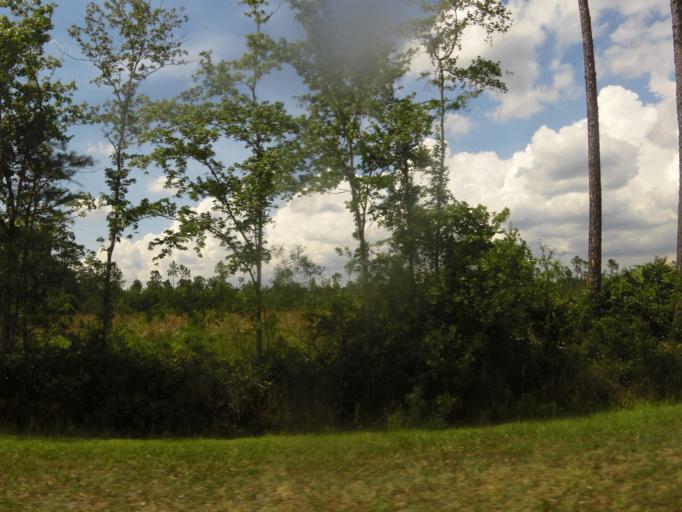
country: US
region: Florida
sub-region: Duval County
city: Baldwin
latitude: 30.2016
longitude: -82.0259
